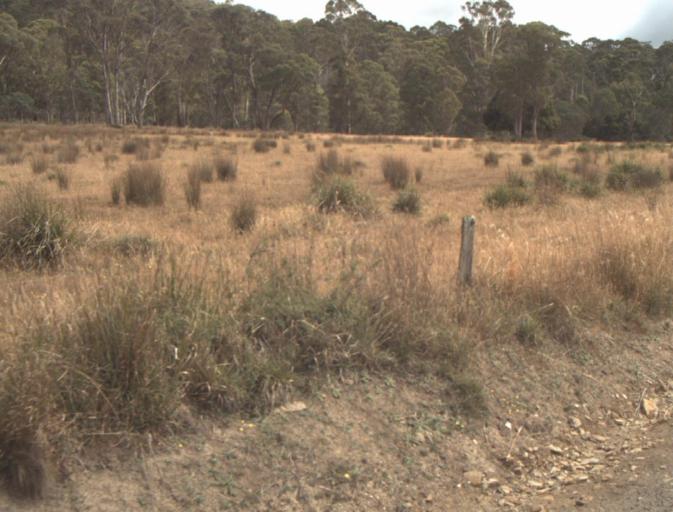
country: AU
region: Tasmania
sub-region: Northern Midlands
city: Evandale
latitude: -41.4690
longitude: 147.4471
